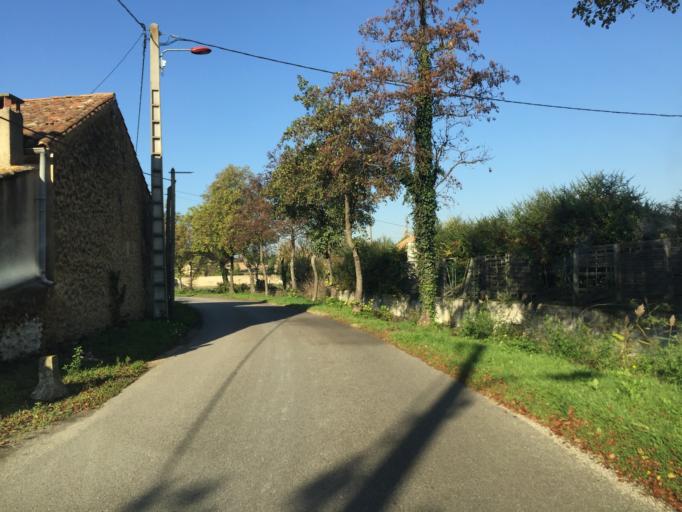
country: FR
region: Provence-Alpes-Cote d'Azur
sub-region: Departement du Vaucluse
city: Entraigues-sur-la-Sorgue
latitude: 44.0070
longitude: 4.9234
